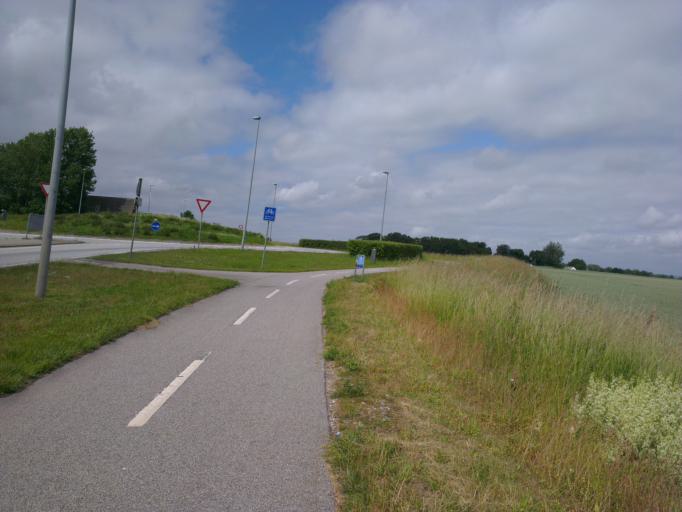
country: DK
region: Zealand
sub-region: Lejre Kommune
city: Lejre
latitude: 55.6557
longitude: 11.9207
